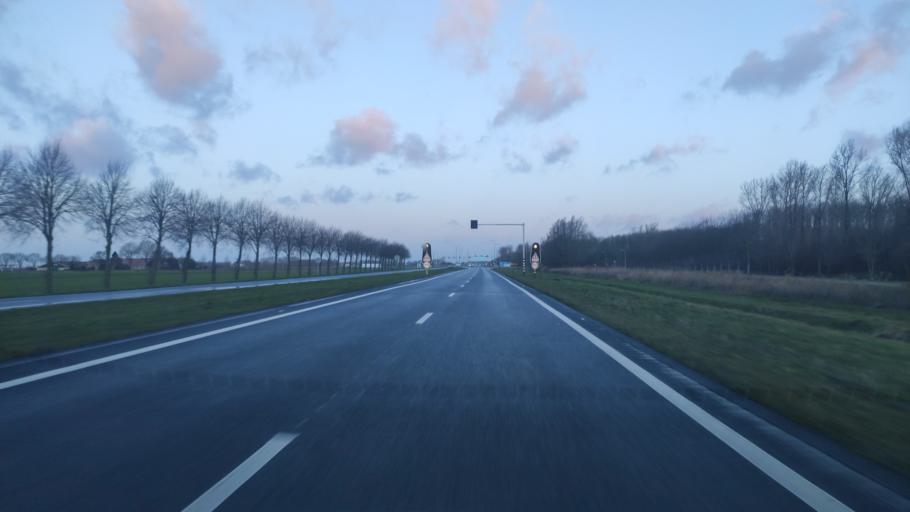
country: NL
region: Flevoland
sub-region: Gemeente Lelystad
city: Lelystad
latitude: 52.4421
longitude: 5.5562
